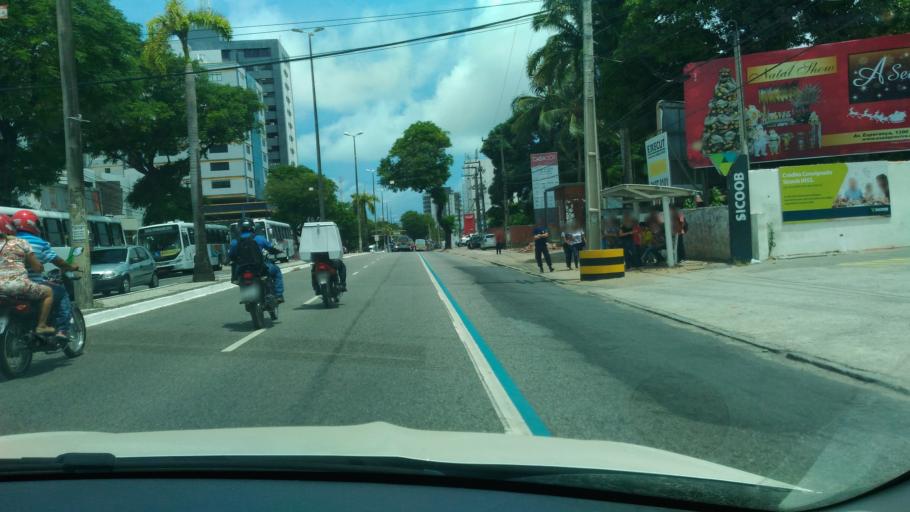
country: BR
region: Paraiba
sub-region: Joao Pessoa
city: Joao Pessoa
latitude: -7.1198
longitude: -34.8612
